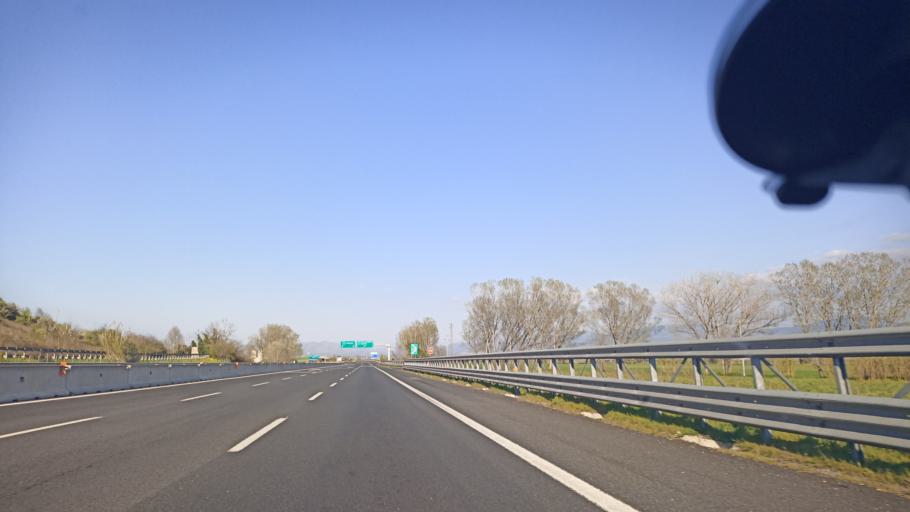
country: IT
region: Latium
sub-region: Citta metropolitana di Roma Capitale
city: Costaroni
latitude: 42.0814
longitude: 12.5552
